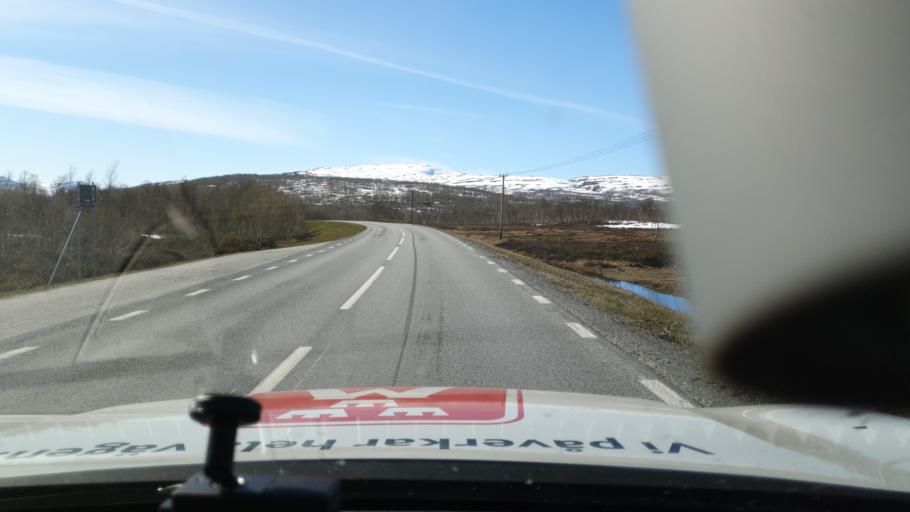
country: NO
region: Nordland
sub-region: Rana
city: Mo i Rana
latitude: 66.0361
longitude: 15.0659
